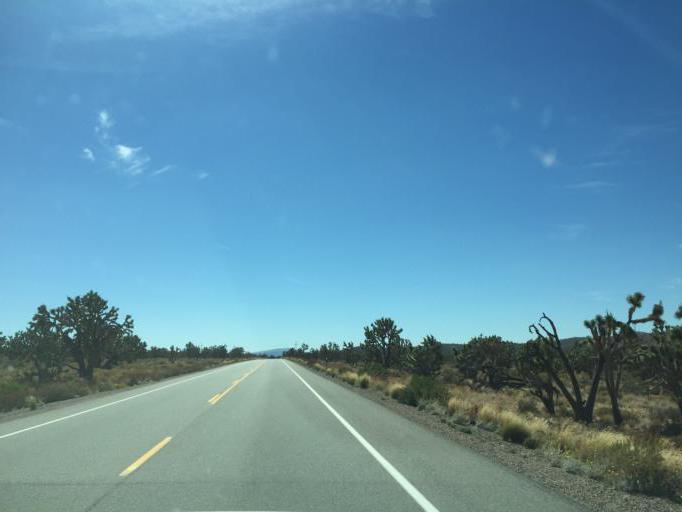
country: US
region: Arizona
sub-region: Mohave County
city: Meadview
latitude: 35.8699
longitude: -114.0653
